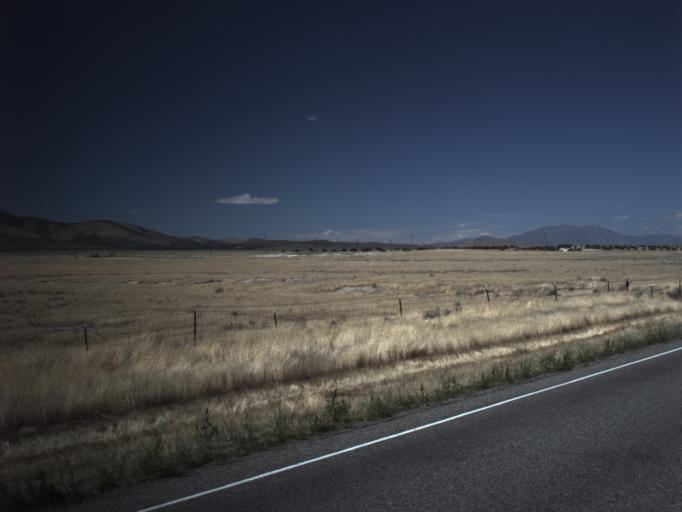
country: US
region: Utah
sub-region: Utah County
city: Genola
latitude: 39.9782
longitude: -111.9570
